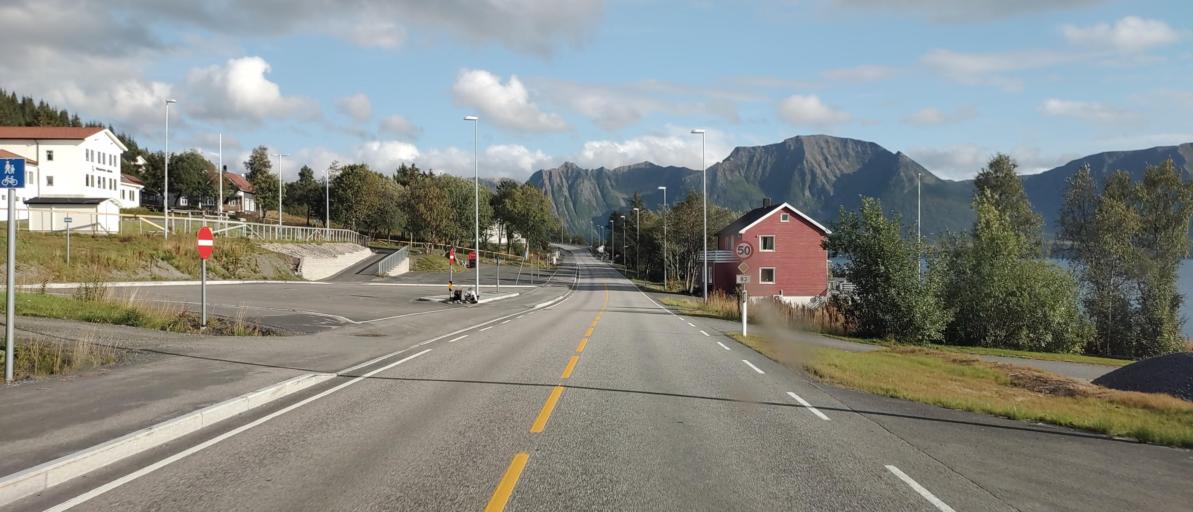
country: NO
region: Nordland
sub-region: Sortland
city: Sortland
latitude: 68.7537
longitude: 15.4688
